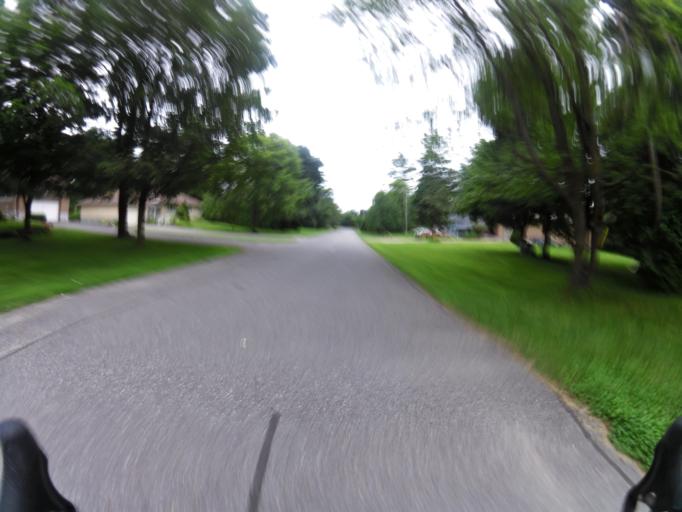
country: CA
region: Ontario
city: Ottawa
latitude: 45.3231
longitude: -75.7145
